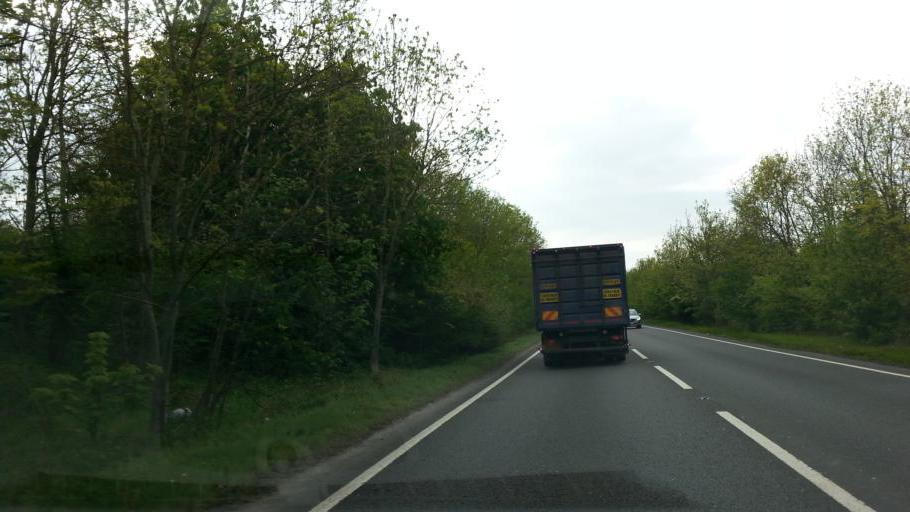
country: GB
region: England
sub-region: Nottinghamshire
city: South Collingham
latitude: 53.0778
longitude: -0.7051
